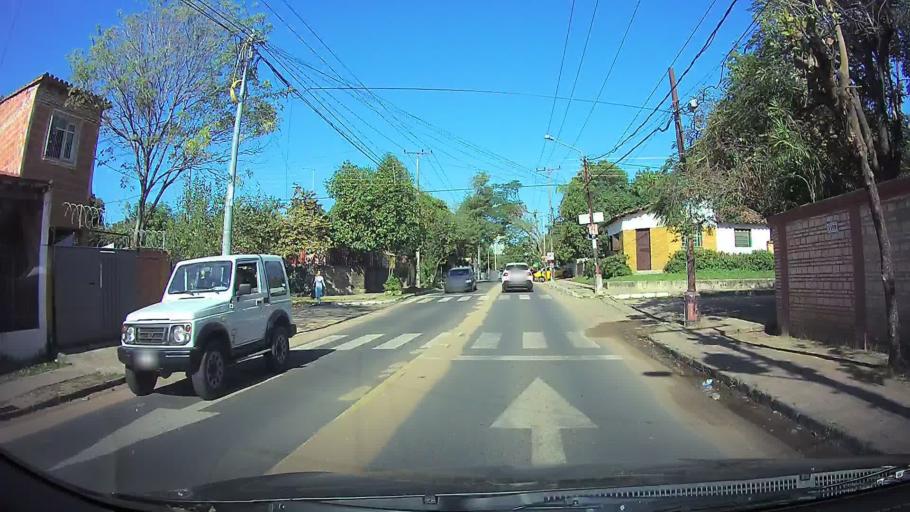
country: PY
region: Asuncion
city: Asuncion
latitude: -25.2521
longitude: -57.5842
